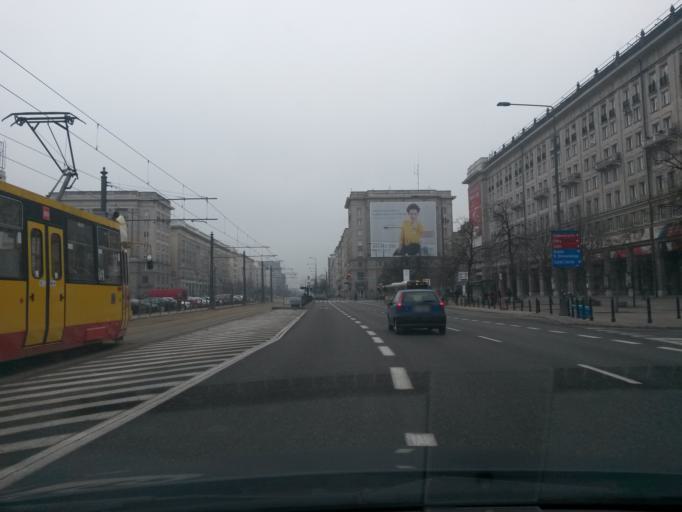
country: PL
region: Masovian Voivodeship
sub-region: Warszawa
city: Srodmiescie
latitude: 52.2219
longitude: 21.0166
